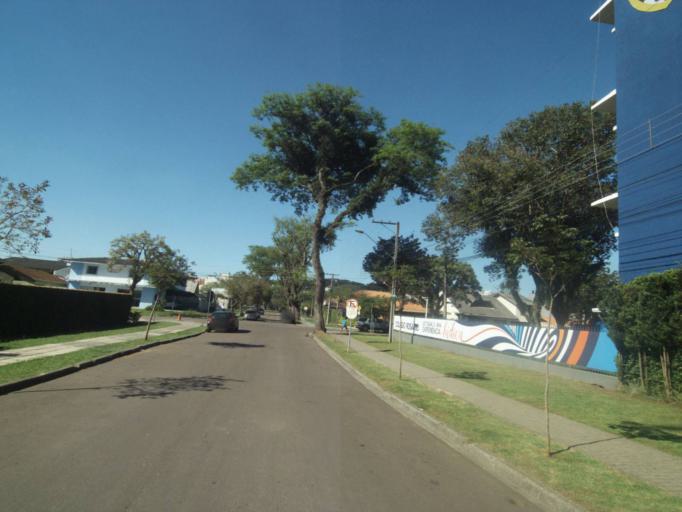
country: BR
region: Parana
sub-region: Curitiba
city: Curitiba
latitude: -25.3906
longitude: -49.2350
